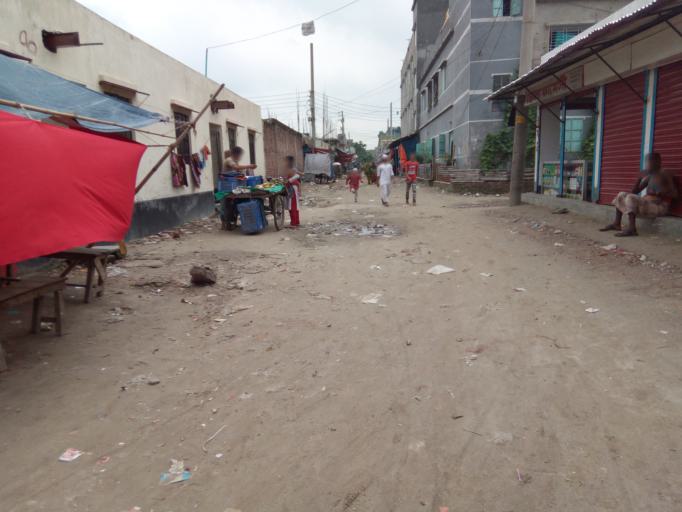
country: BD
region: Dhaka
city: Azimpur
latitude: 23.7586
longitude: 90.3499
